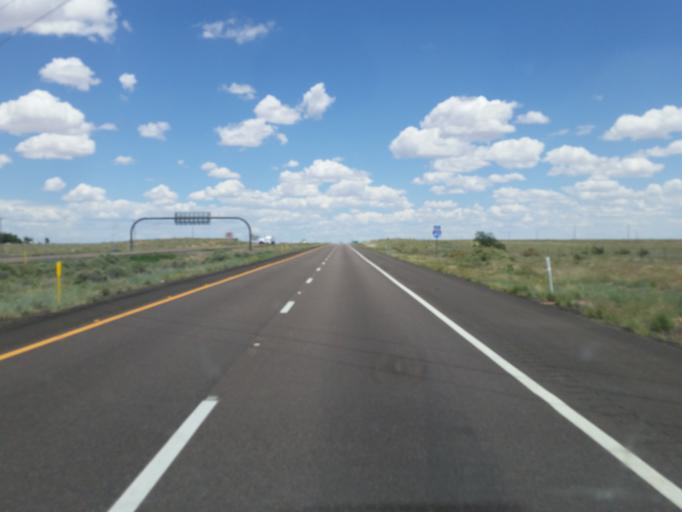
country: US
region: Arizona
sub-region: Navajo County
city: Holbrook
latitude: 34.9815
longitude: -110.0490
